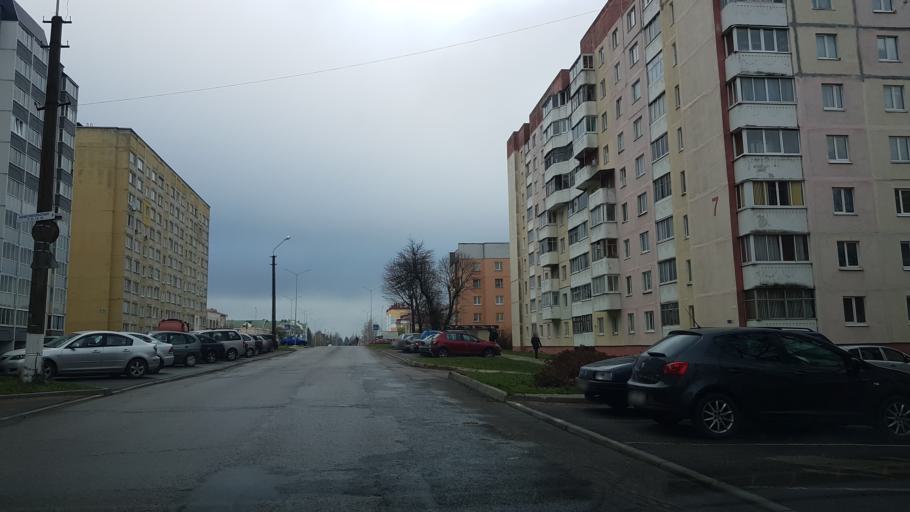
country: BY
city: Fanipol
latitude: 53.7482
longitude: 27.3280
